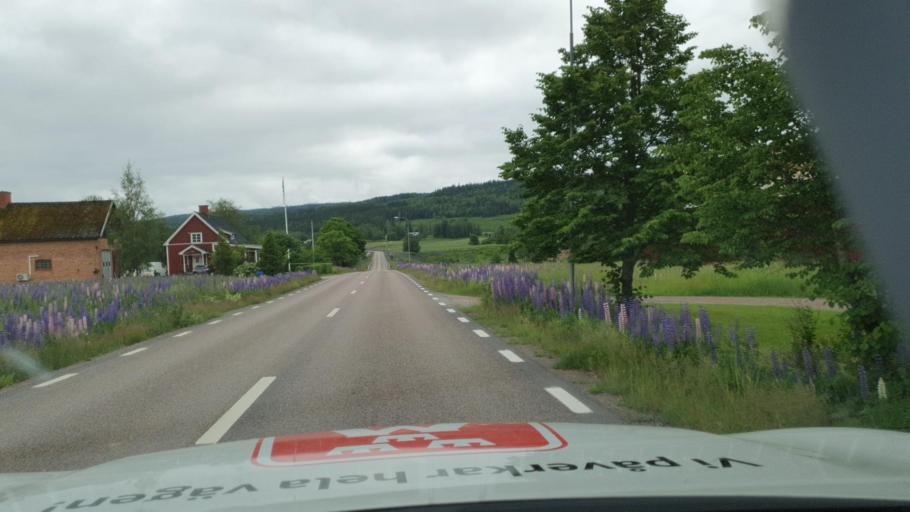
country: SE
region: Vaermland
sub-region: Sunne Kommun
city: Sunne
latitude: 59.8547
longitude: 12.9454
